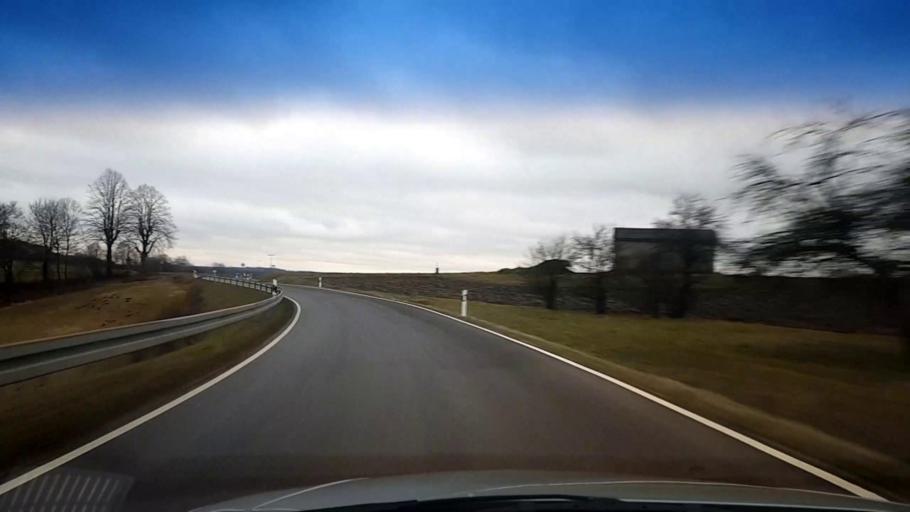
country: DE
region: Bavaria
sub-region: Upper Franconia
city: Wattendorf
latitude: 50.0284
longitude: 11.0653
